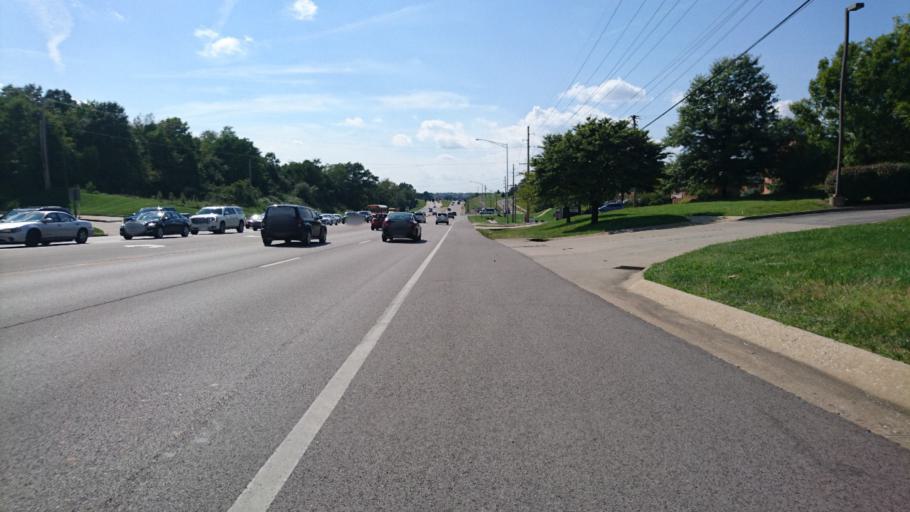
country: US
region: Missouri
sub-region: Saint Louis County
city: Ellisville
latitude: 38.5905
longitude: -90.5961
